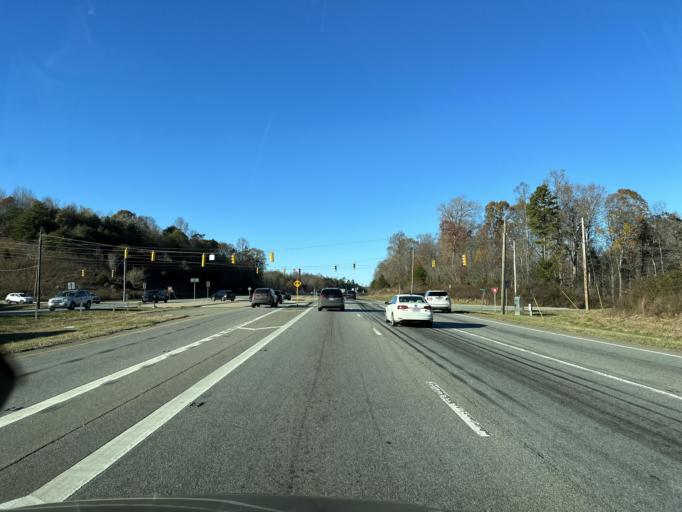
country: US
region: North Carolina
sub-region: Lincoln County
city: Westport
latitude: 35.4770
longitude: -81.0125
